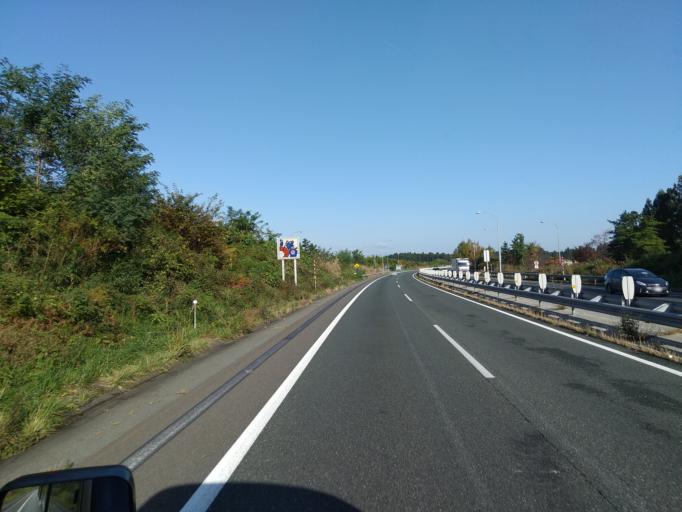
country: JP
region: Iwate
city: Mizusawa
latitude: 39.0691
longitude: 141.1009
